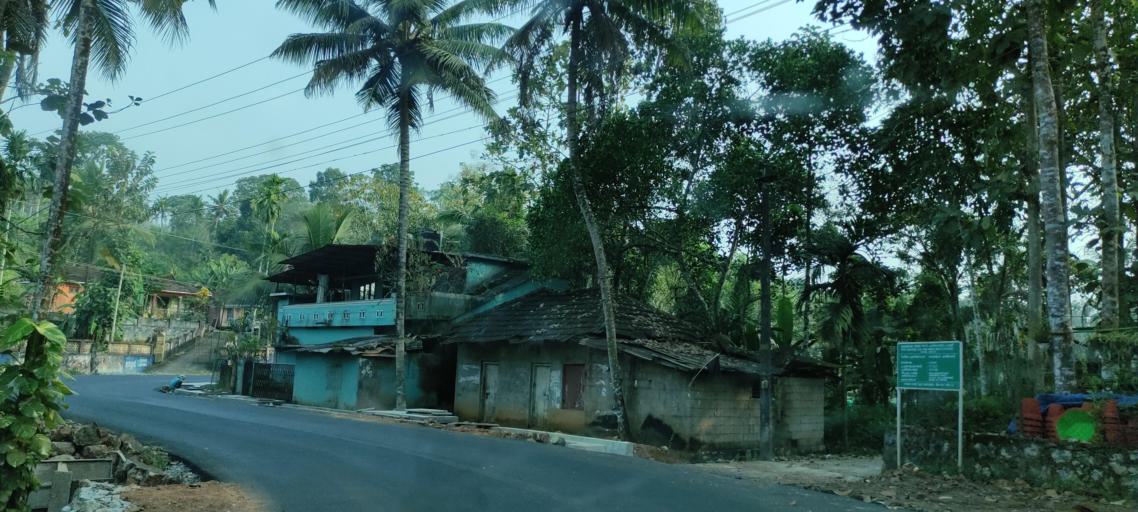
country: IN
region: Kerala
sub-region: Pattanamtitta
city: Adur
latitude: 9.1066
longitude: 76.7267
